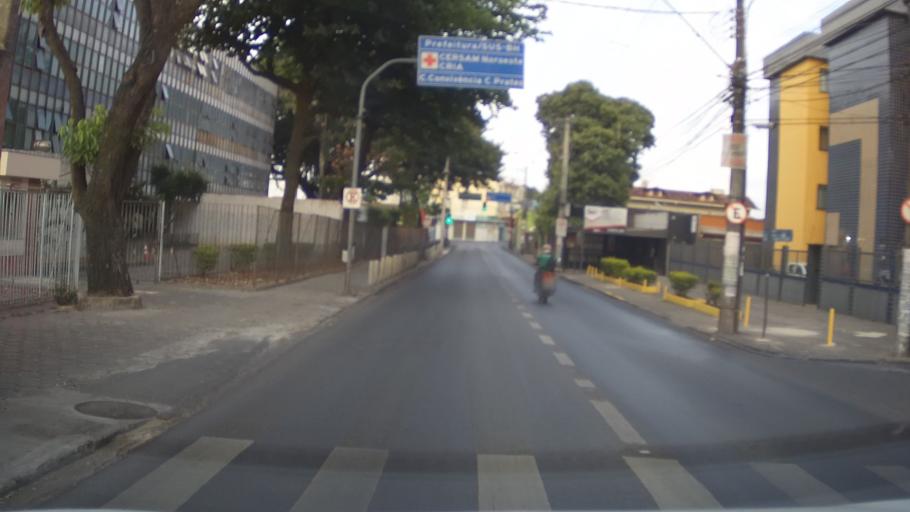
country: BR
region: Minas Gerais
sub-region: Belo Horizonte
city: Belo Horizonte
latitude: -19.9149
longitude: -43.9703
